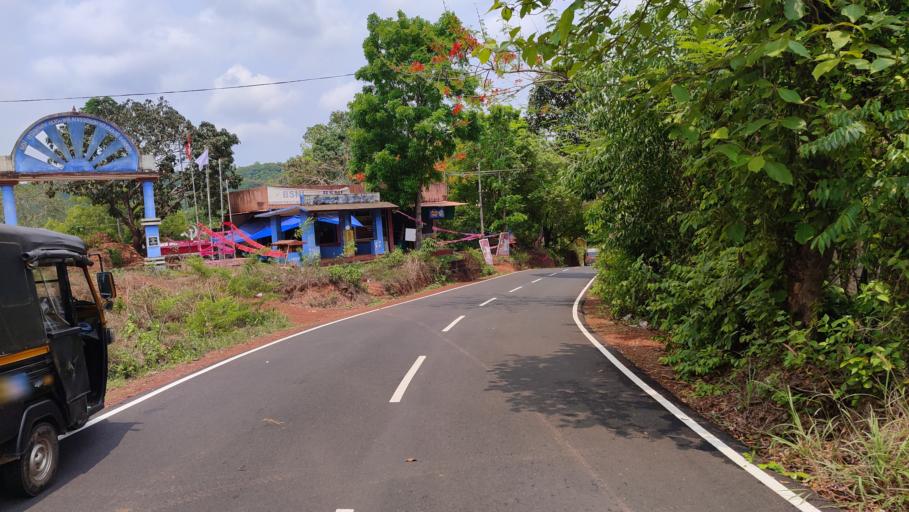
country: IN
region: Kerala
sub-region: Kasaragod District
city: Kannangad
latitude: 12.3211
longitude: 75.1362
